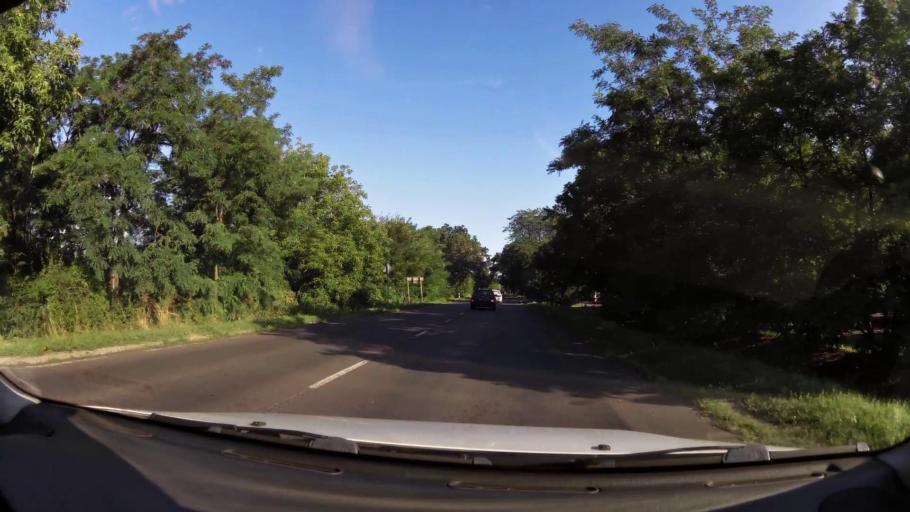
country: HU
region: Pest
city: Nyaregyhaza
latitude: 47.3105
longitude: 19.4977
